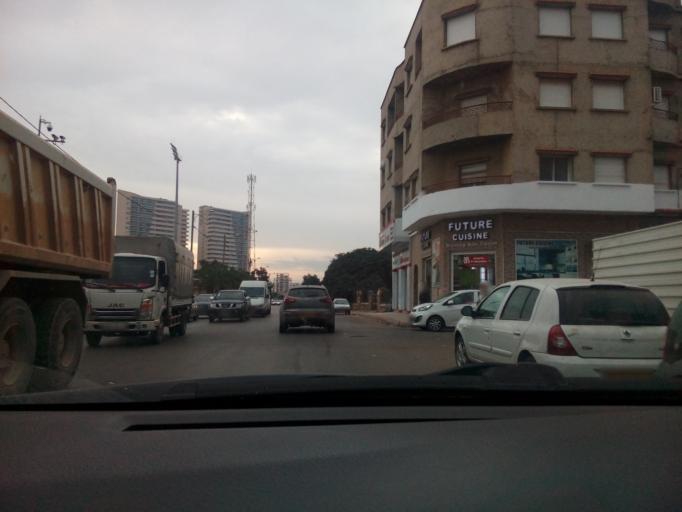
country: DZ
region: Oran
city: Oran
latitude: 35.6838
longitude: -0.6387
